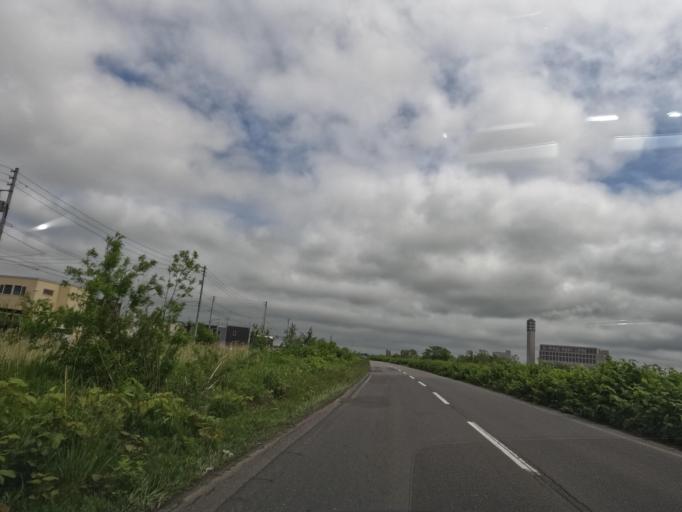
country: JP
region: Hokkaido
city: Sapporo
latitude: 43.0900
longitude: 141.4297
